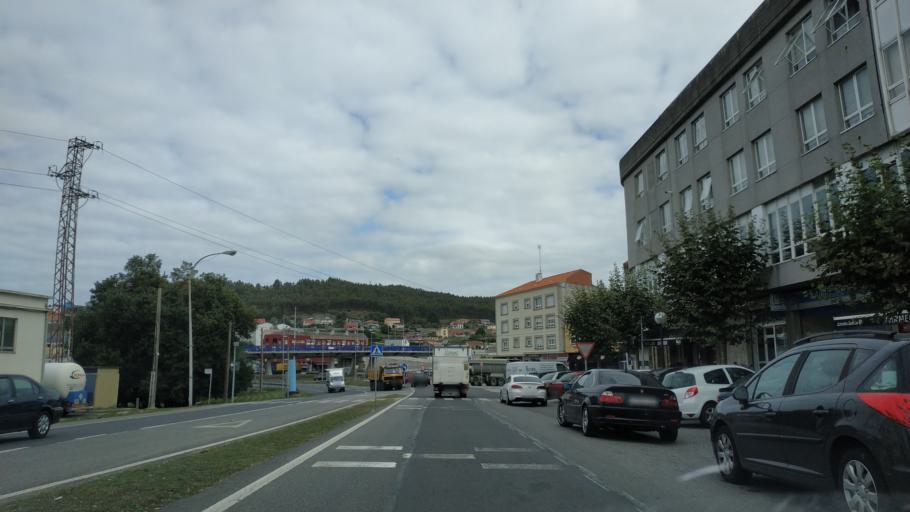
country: ES
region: Galicia
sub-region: Provincia da Coruna
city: Arteixo
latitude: 43.3160
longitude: -8.4920
